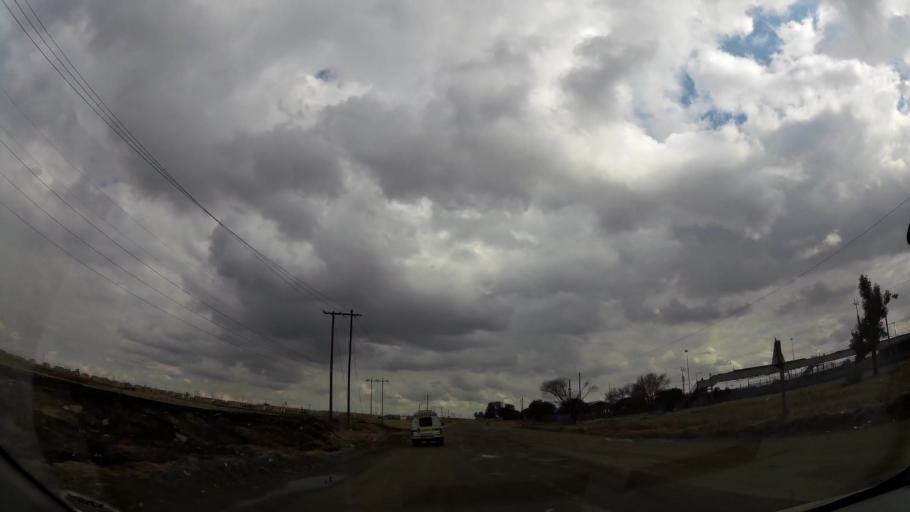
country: ZA
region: Orange Free State
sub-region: Fezile Dabi District Municipality
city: Sasolburg
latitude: -26.8541
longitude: 27.8676
